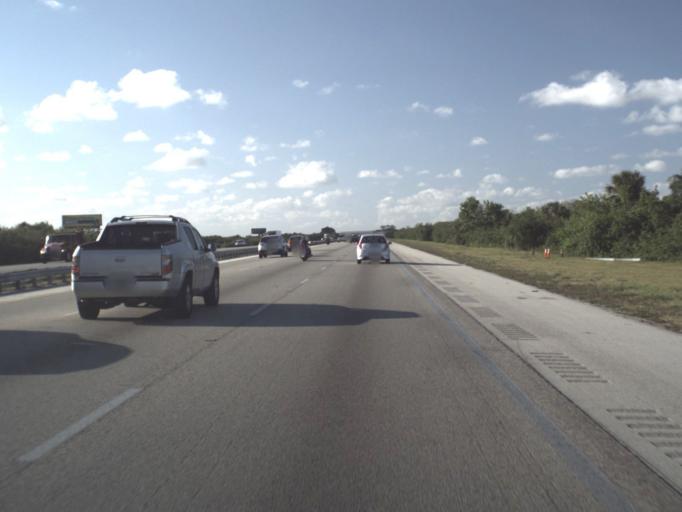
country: US
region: Florida
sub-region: Brevard County
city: Rockledge
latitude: 28.2530
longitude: -80.7249
